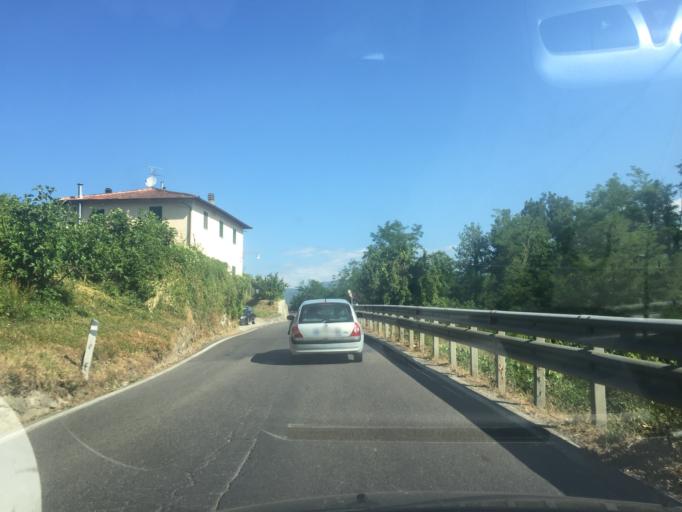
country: IT
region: Tuscany
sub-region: Provincia di Lucca
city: Castelnuovo di Garfagnana
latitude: 44.1255
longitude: 10.3871
